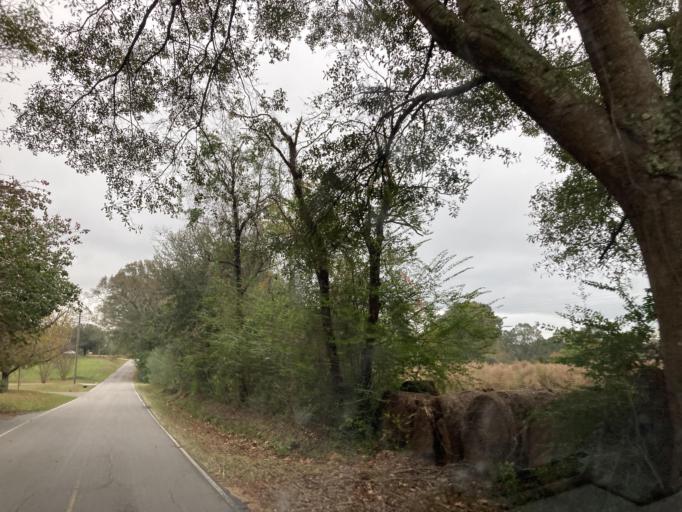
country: US
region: Mississippi
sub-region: Lamar County
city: Purvis
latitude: 31.2041
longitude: -89.4412
